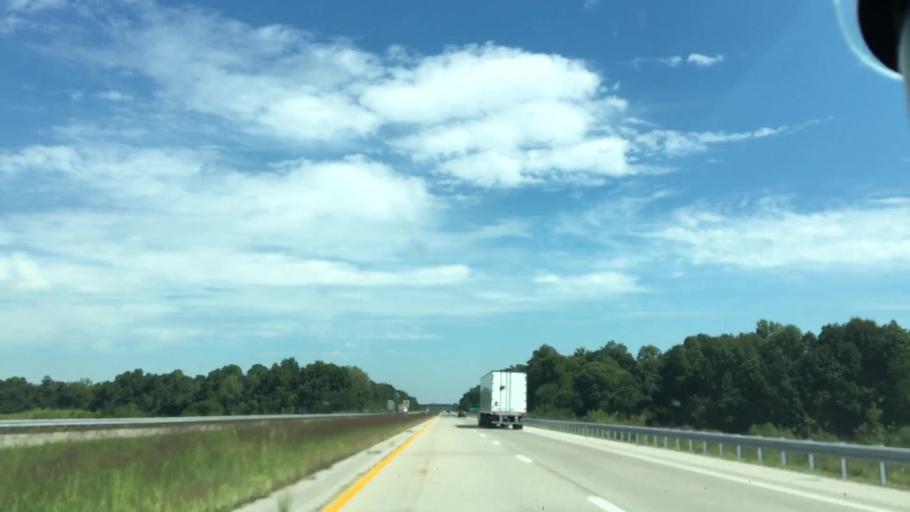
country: US
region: Kentucky
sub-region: Daviess County
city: Owensboro
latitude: 37.7598
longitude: -87.2448
